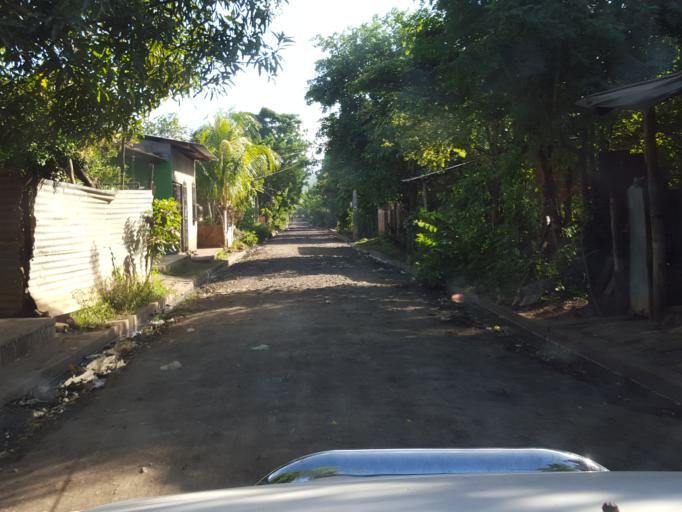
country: NI
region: Leon
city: Leon
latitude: 12.4245
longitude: -86.9080
